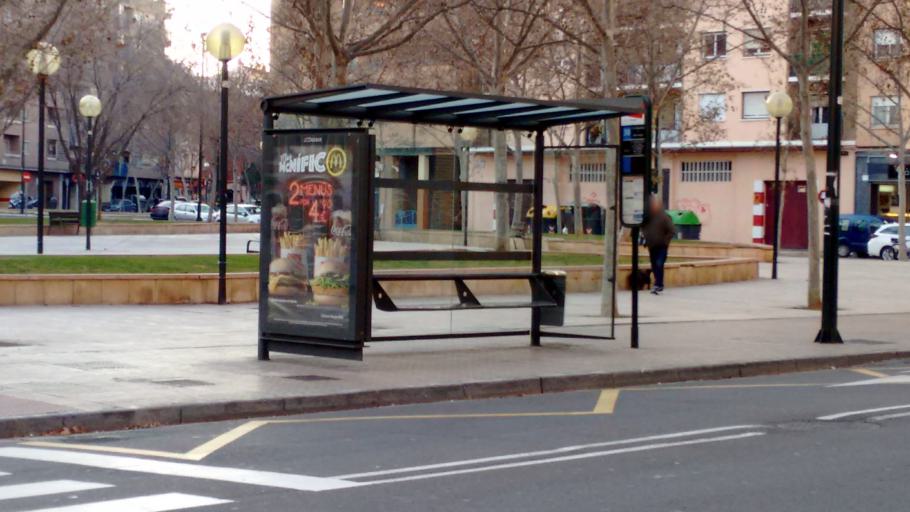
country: ES
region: Aragon
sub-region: Provincia de Zaragoza
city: Zaragoza
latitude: 41.6413
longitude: -0.8674
